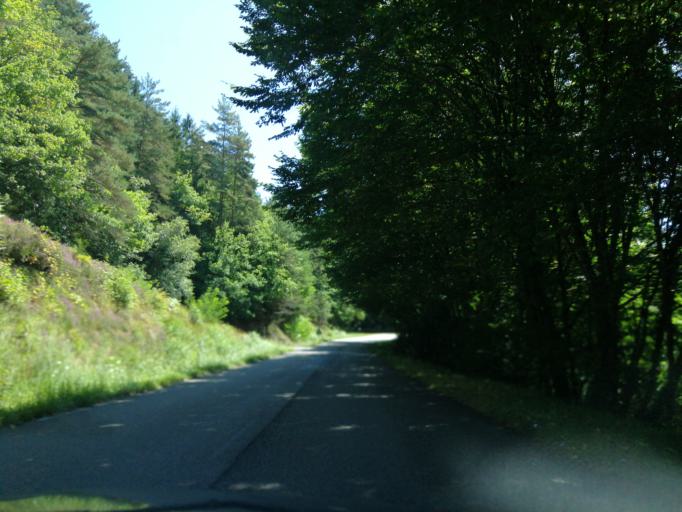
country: FR
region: Limousin
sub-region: Departement de la Correze
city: Argentat
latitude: 45.0543
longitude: 1.9481
